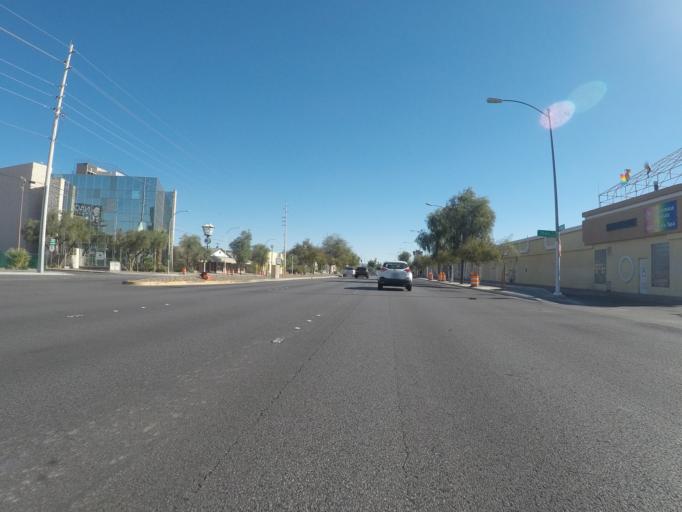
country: US
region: Nevada
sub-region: Clark County
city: Winchester
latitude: 36.1443
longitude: -115.1453
